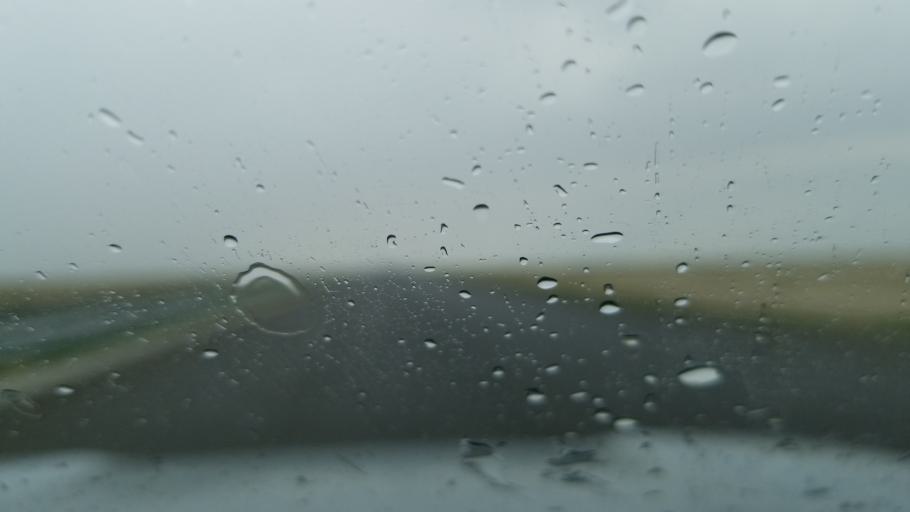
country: TM
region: Balkan
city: Serdar
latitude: 39.0141
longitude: 56.2270
